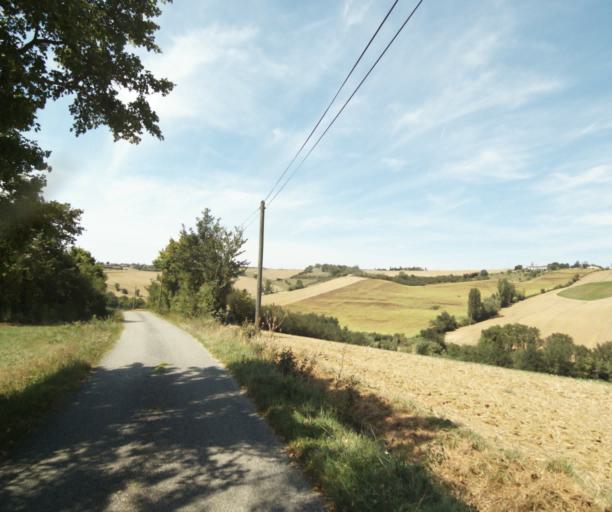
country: FR
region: Midi-Pyrenees
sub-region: Departement de la Haute-Garonne
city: Gaillac-Toulza
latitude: 43.2324
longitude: 1.4051
